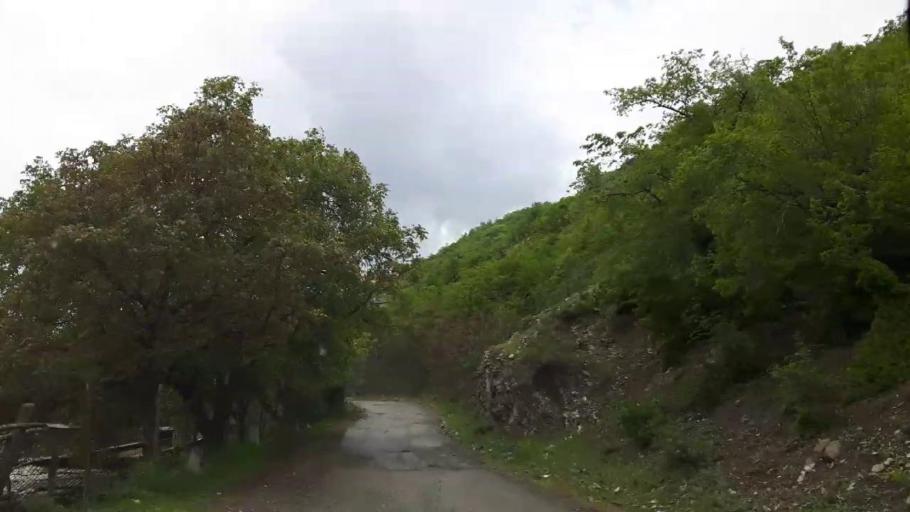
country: GE
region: Shida Kartli
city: Gori
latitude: 41.8879
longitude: 43.9999
